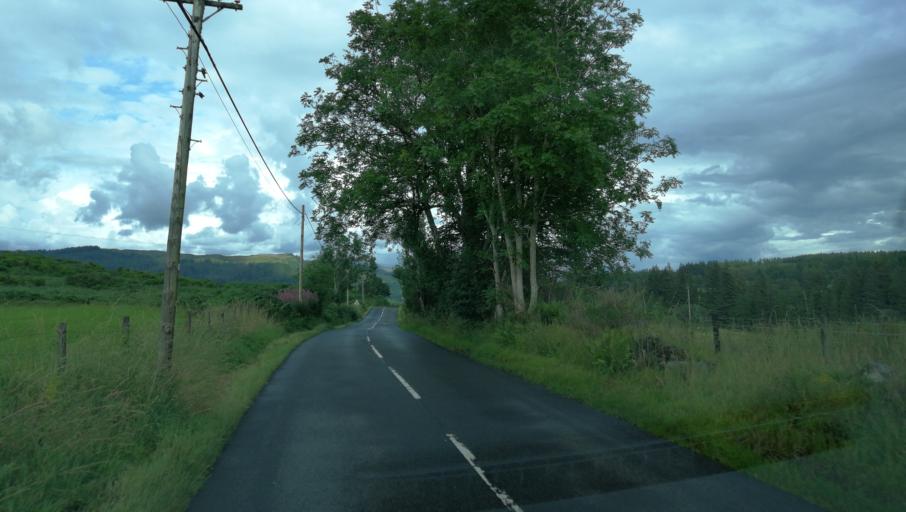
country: GB
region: Scotland
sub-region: Stirling
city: Callander
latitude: 56.2336
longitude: -4.2650
